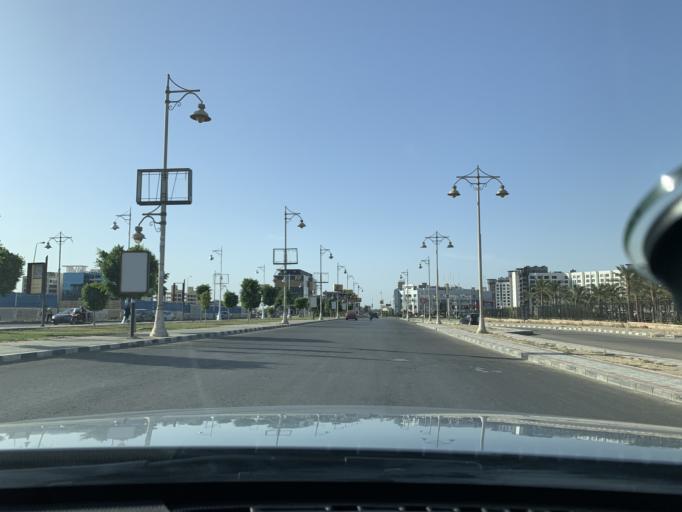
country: EG
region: Muhafazat al Qalyubiyah
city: Al Khankah
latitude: 30.0227
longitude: 31.4957
